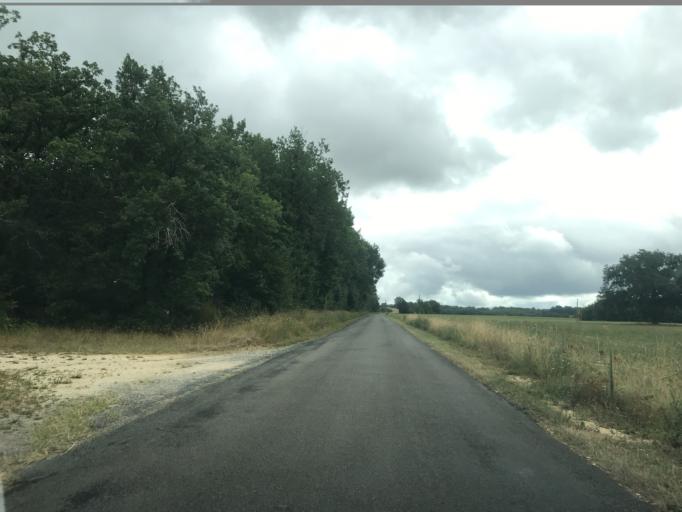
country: FR
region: Poitou-Charentes
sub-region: Departement de la Charente
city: Dignac
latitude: 45.5575
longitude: 0.2453
